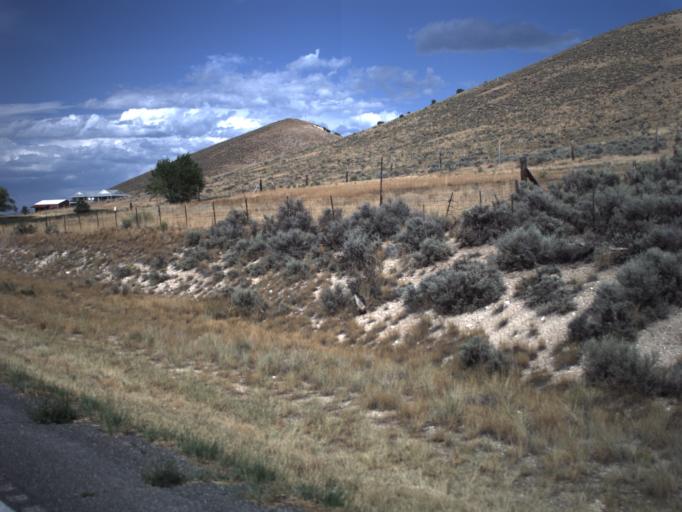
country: US
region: Utah
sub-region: Sanpete County
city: Manti
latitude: 39.2087
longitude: -111.6900
